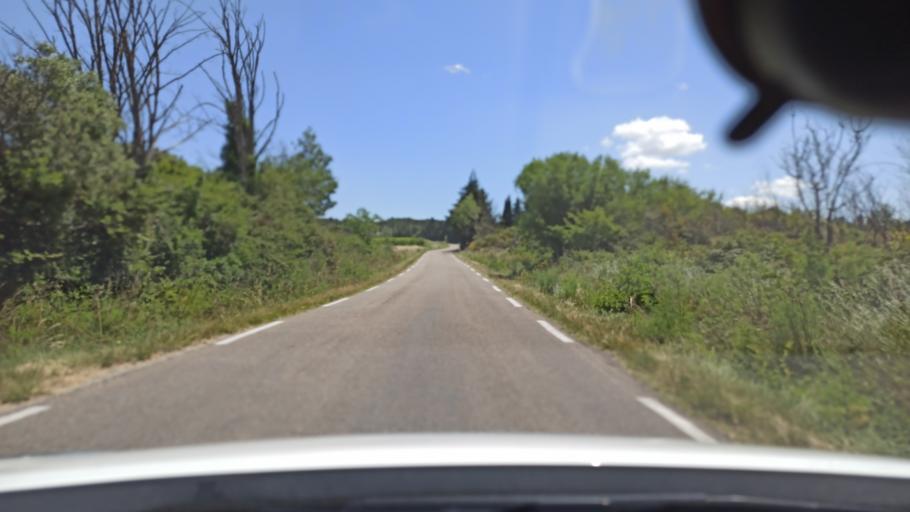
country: FR
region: Provence-Alpes-Cote d'Azur
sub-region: Departement du Vaucluse
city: Chateauneuf-de-Gadagne
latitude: 43.9096
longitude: 4.9176
